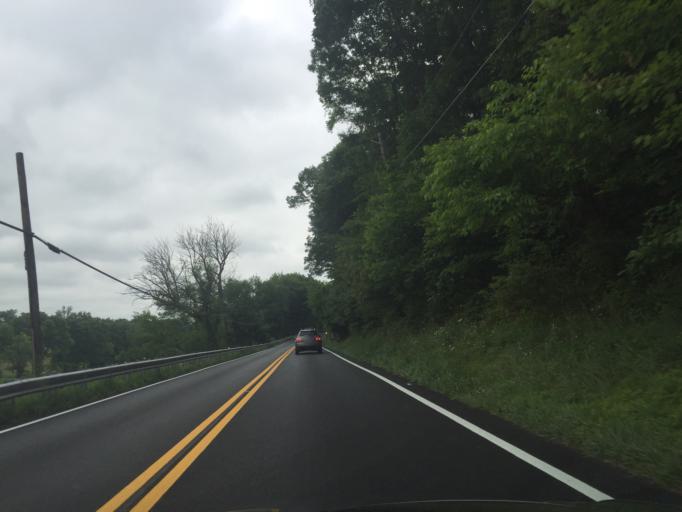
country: US
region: Maryland
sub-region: Baltimore County
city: Hunt Valley
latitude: 39.5323
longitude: -76.5509
